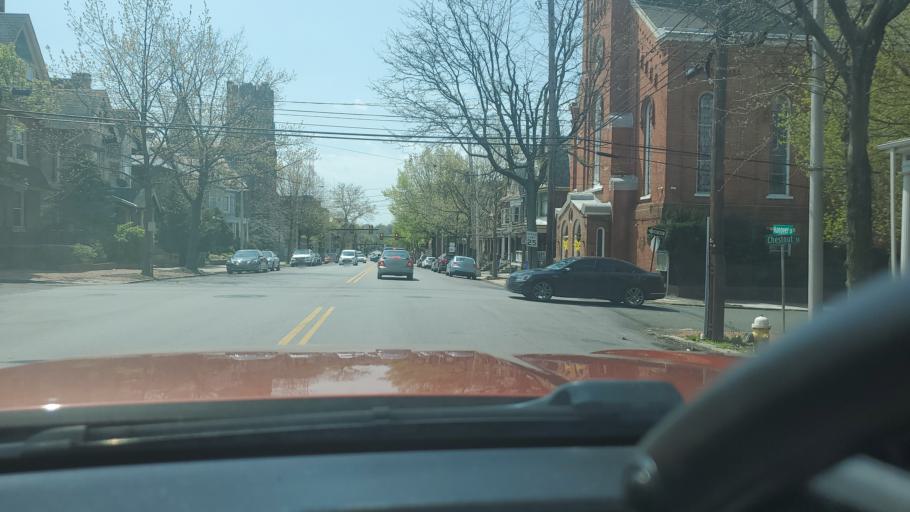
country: US
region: Pennsylvania
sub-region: Montgomery County
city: Pottstown
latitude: 40.2479
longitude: -75.6500
